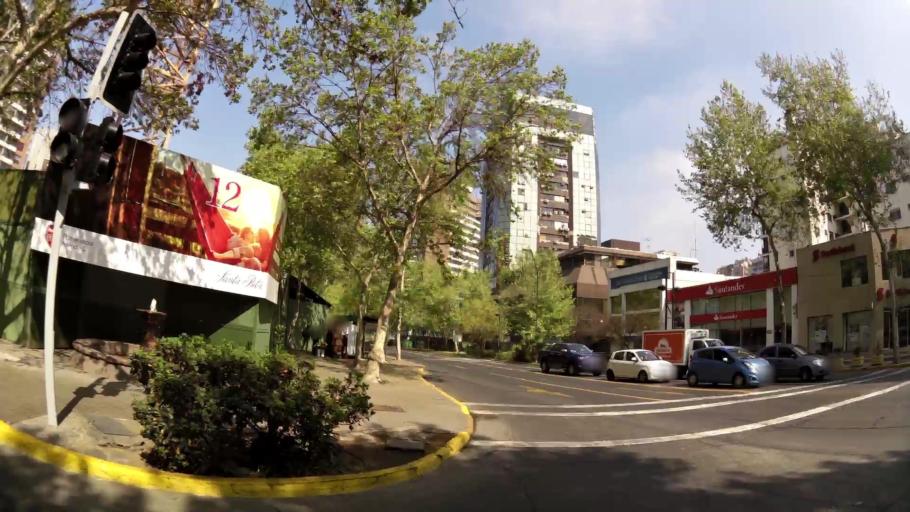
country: CL
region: Santiago Metropolitan
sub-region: Provincia de Santiago
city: Villa Presidente Frei, Nunoa, Santiago, Chile
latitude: -33.4215
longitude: -70.6077
